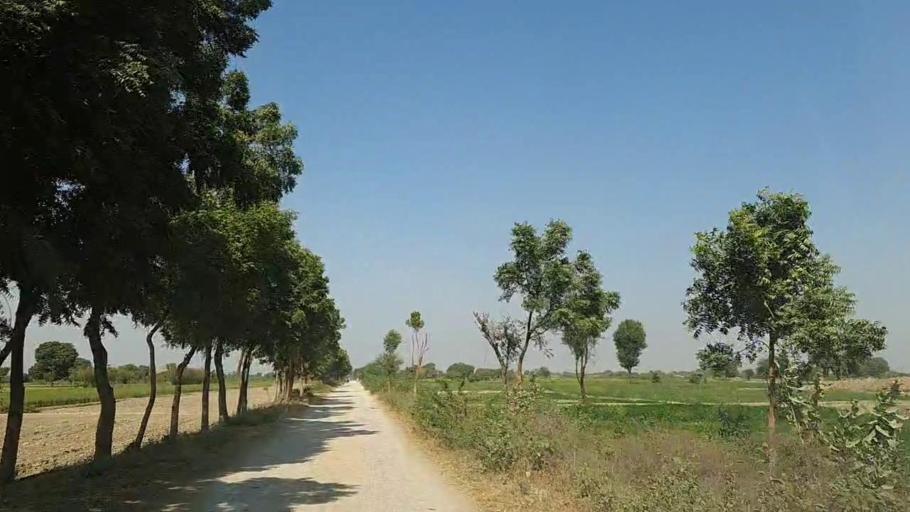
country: PK
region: Sindh
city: Naukot
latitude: 24.8670
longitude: 69.4037
